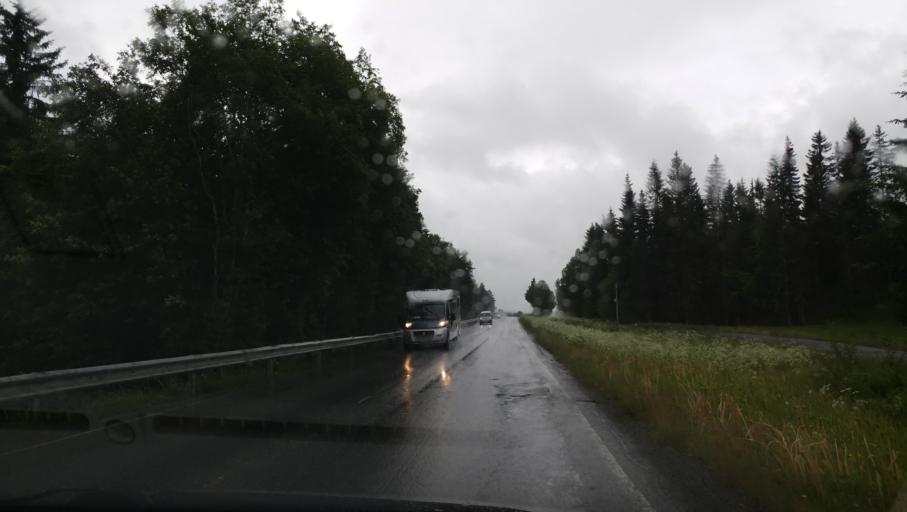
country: NO
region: Sor-Trondelag
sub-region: Selbu
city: Mebonden
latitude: 63.2936
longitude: 11.0761
